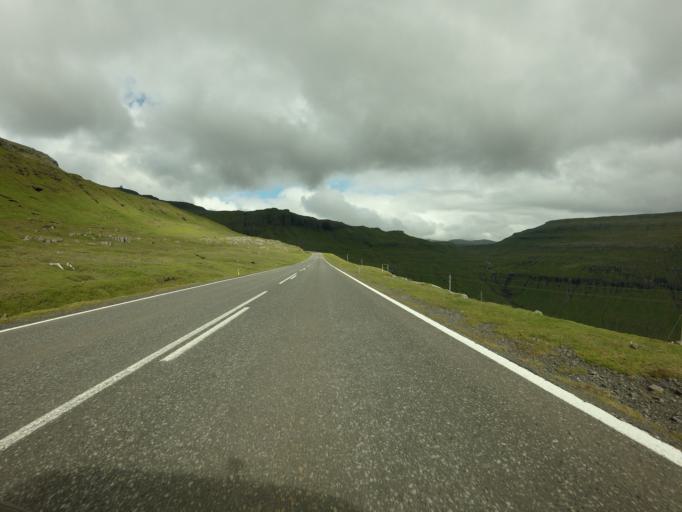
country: FO
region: Streymoy
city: Kollafjordhur
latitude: 62.0621
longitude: -6.9278
